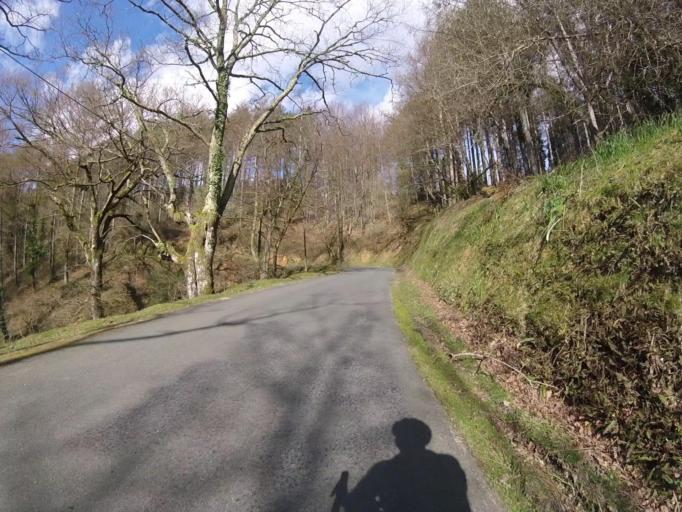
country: ES
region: Navarre
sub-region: Provincia de Navarra
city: Etxalar
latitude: 43.2626
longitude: -1.6090
